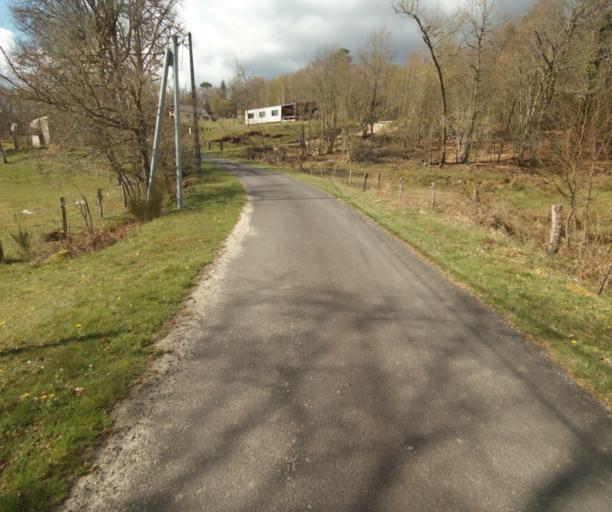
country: FR
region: Limousin
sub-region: Departement de la Correze
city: Argentat
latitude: 45.2383
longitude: 1.9531
